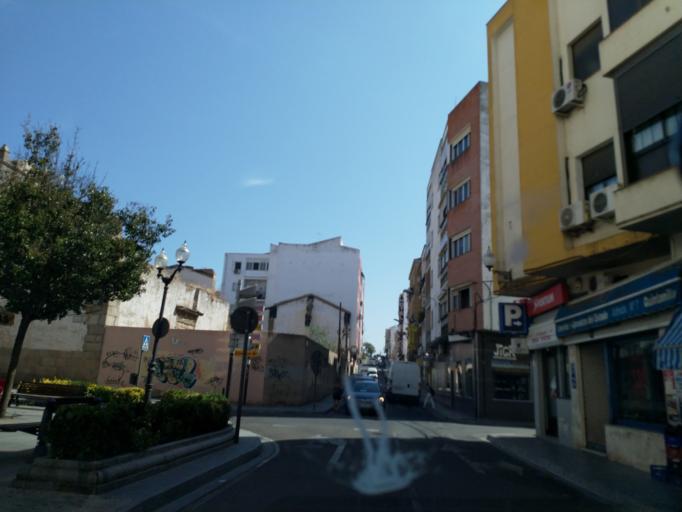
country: ES
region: Extremadura
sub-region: Provincia de Badajoz
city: Merida
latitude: 38.9138
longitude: -6.3449
